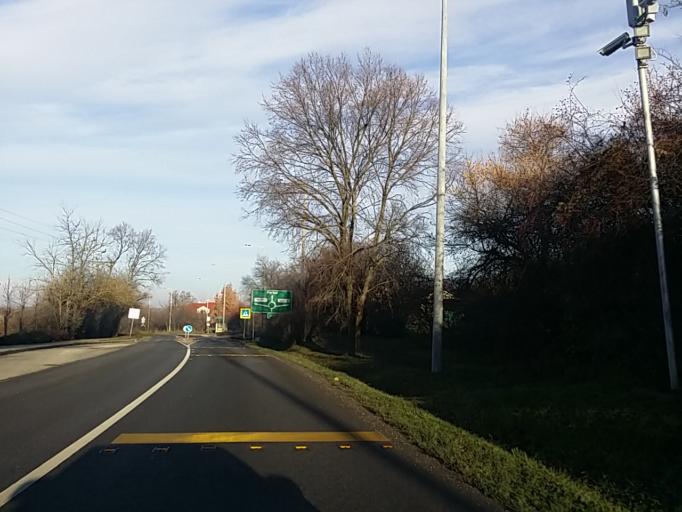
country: HU
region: Pest
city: Telki
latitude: 47.5417
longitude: 18.8349
